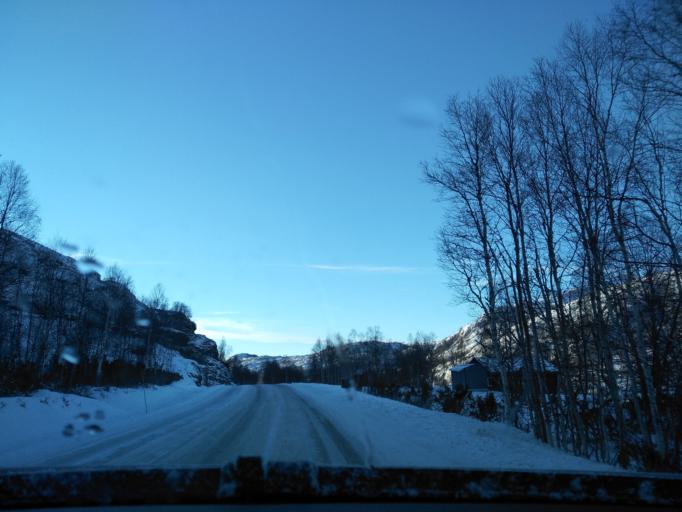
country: NO
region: Vest-Agder
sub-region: Sirdal
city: Tonstad
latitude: 59.0111
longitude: 6.9364
